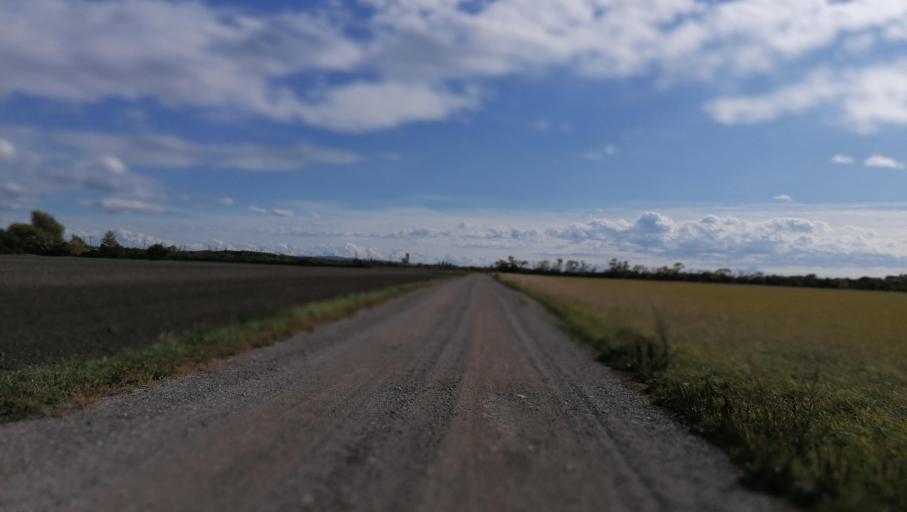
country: AT
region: Lower Austria
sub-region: Politischer Bezirk Baden
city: Teesdorf
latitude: 47.9721
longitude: 16.2843
